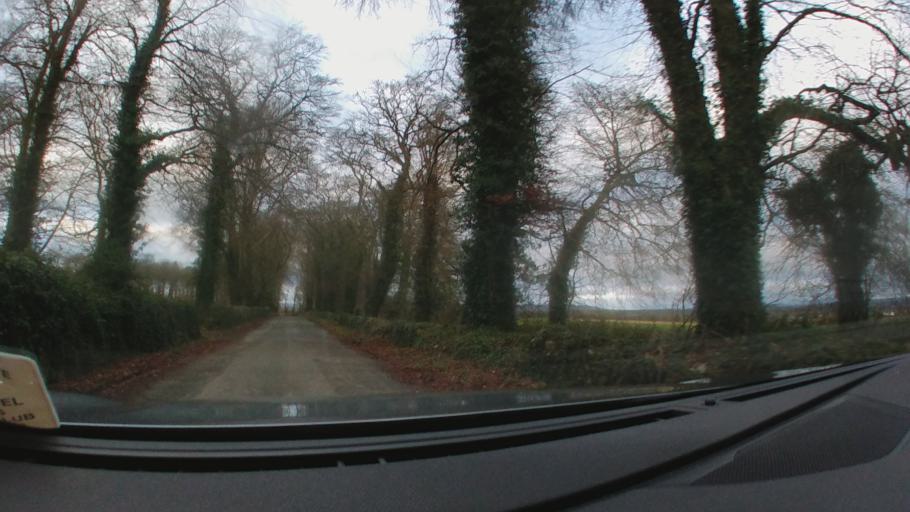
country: IE
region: Leinster
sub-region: Kilkenny
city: Thomastown
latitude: 52.5621
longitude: -7.1397
